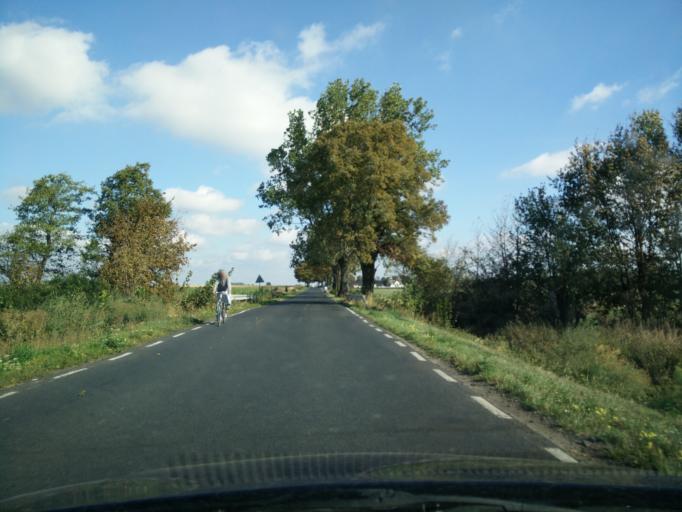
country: PL
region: Greater Poland Voivodeship
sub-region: Powiat sredzki
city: Sroda Wielkopolska
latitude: 52.2573
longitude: 17.3014
